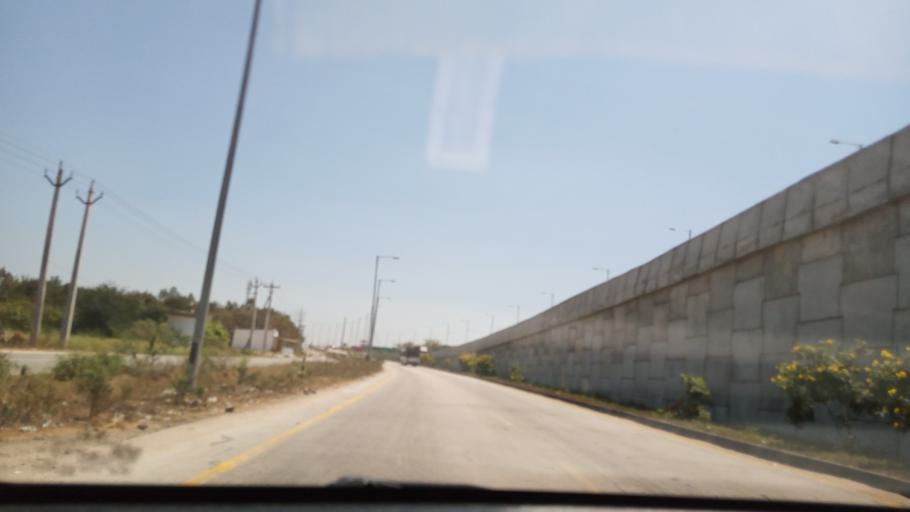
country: IN
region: Andhra Pradesh
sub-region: Chittoor
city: Chittoor
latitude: 13.2046
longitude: 78.9371
